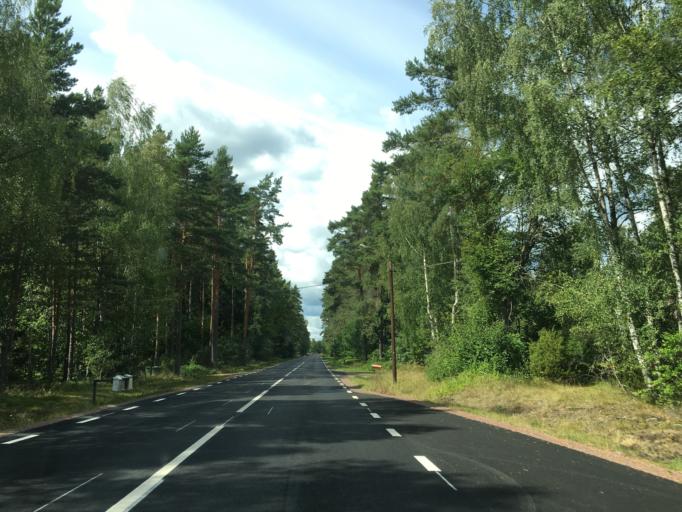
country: SE
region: Kalmar
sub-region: Nybro Kommun
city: Nybro
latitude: 56.9193
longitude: 15.9636
